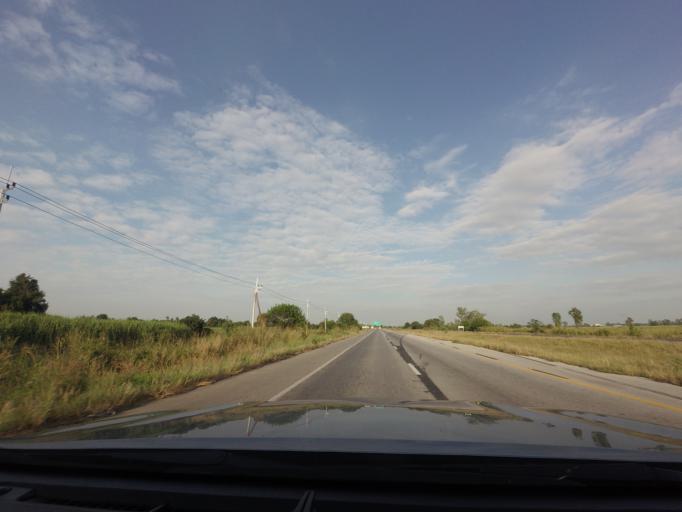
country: TH
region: Nakhon Sawan
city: Nakhon Sawan
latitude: 15.7624
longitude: 100.0986
